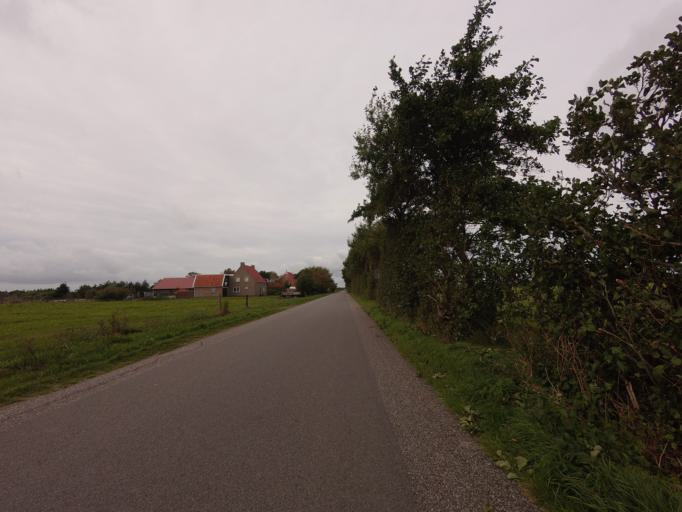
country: NL
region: Friesland
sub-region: Gemeente Ameland
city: Nes
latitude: 53.4401
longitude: 5.7118
